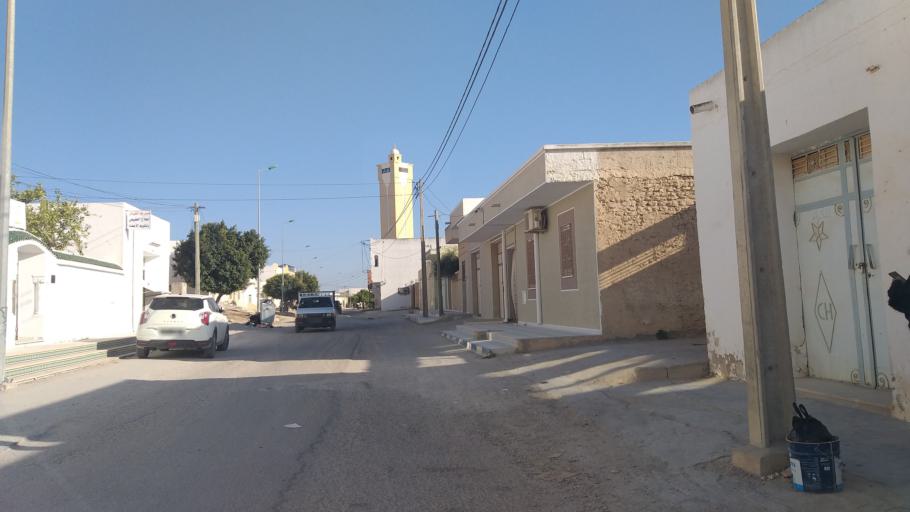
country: TN
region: Al Mahdiyah
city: El Jem
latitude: 35.2890
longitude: 10.7078
